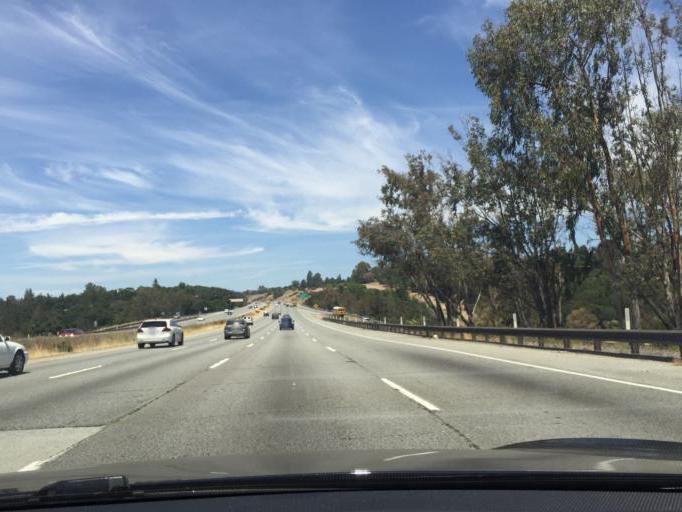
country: US
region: California
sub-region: San Mateo County
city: Woodside
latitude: 37.4356
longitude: -122.2433
